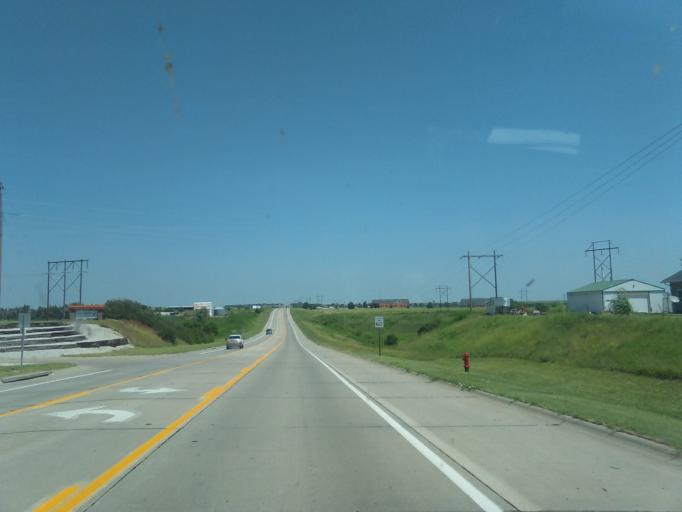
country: US
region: Nebraska
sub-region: Red Willow County
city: McCook
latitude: 40.2218
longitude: -100.6500
